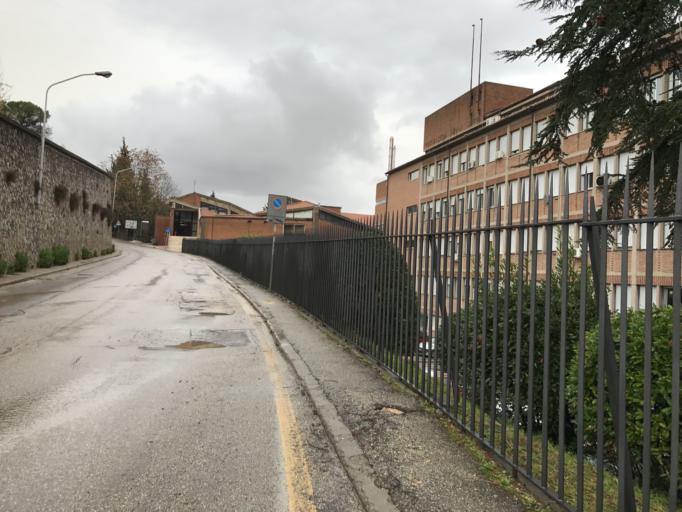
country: IT
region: Umbria
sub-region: Provincia di Perugia
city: Perugia
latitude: 43.1128
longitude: 12.4030
